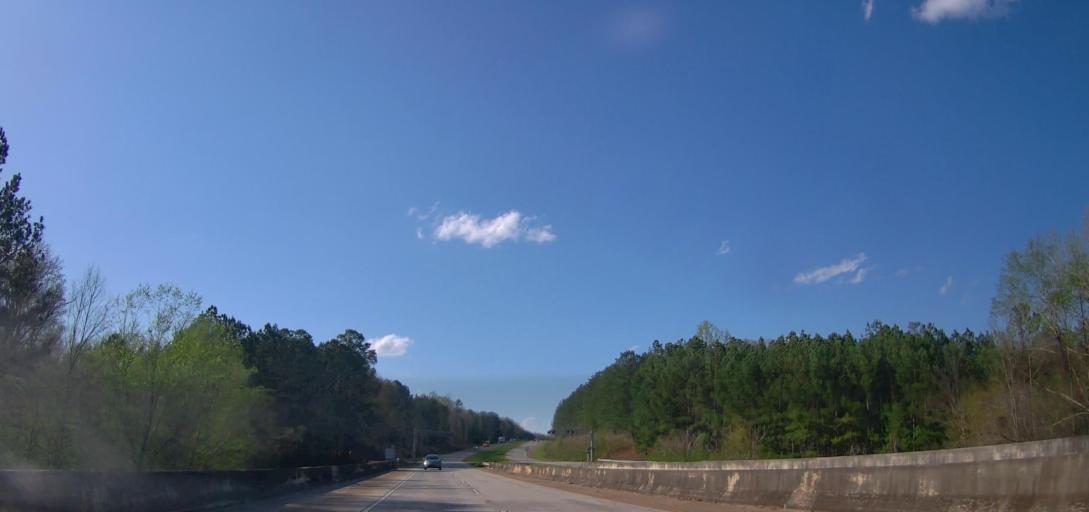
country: US
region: Georgia
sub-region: Baldwin County
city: Hardwick
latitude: 33.0337
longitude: -83.2502
